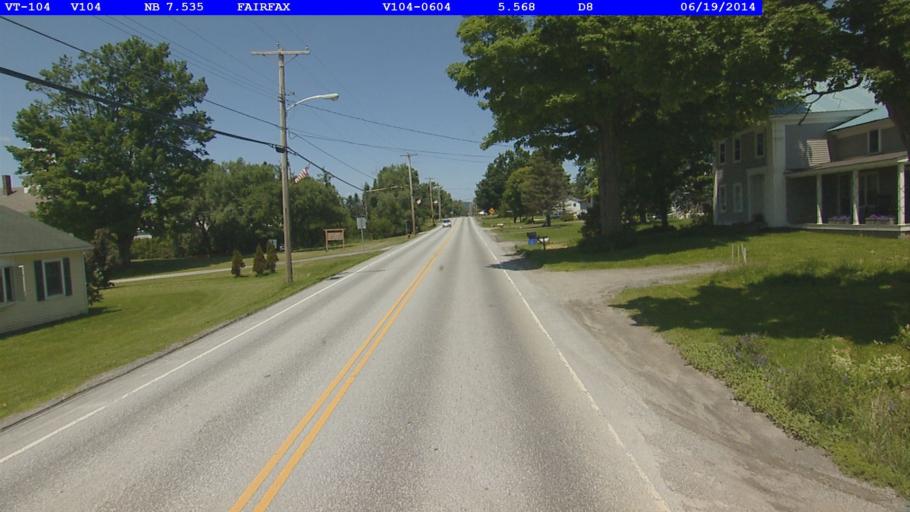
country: US
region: Vermont
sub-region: Chittenden County
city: Milton
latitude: 44.6693
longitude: -73.0136
